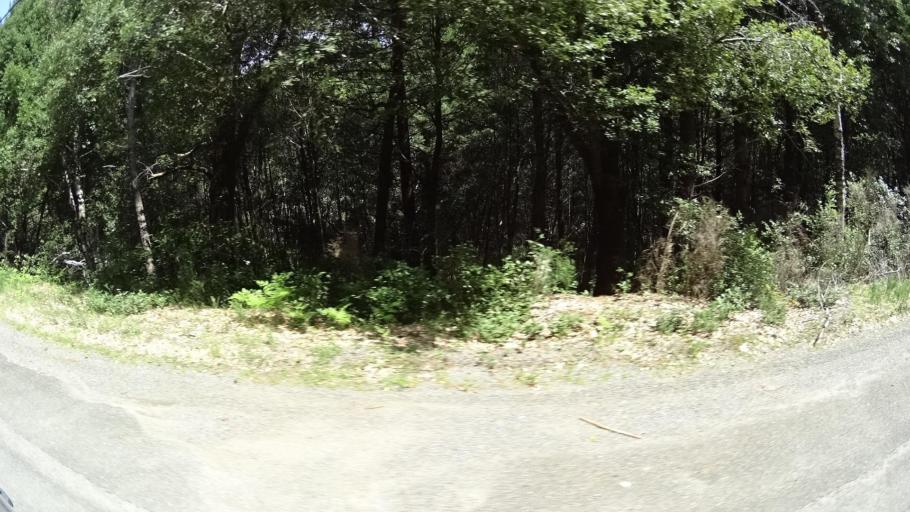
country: US
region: California
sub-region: Humboldt County
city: Redway
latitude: 40.0714
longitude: -123.9578
